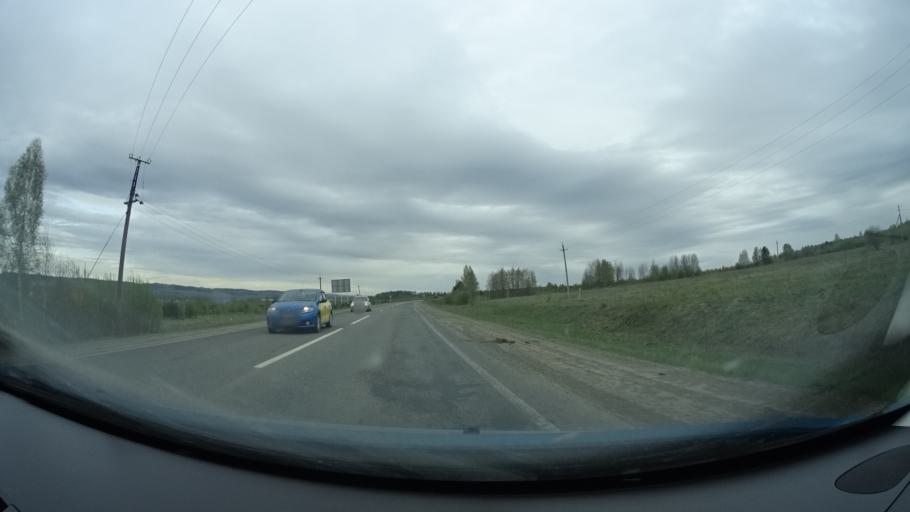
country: RU
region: Perm
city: Osa
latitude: 57.1760
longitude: 55.5320
